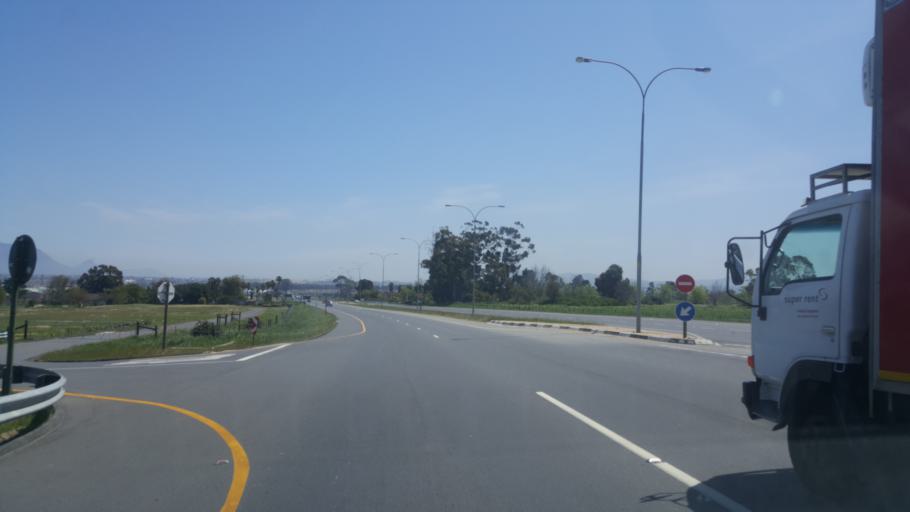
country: ZA
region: Western Cape
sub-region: City of Cape Town
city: Kraaifontein
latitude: -33.9526
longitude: 18.7161
